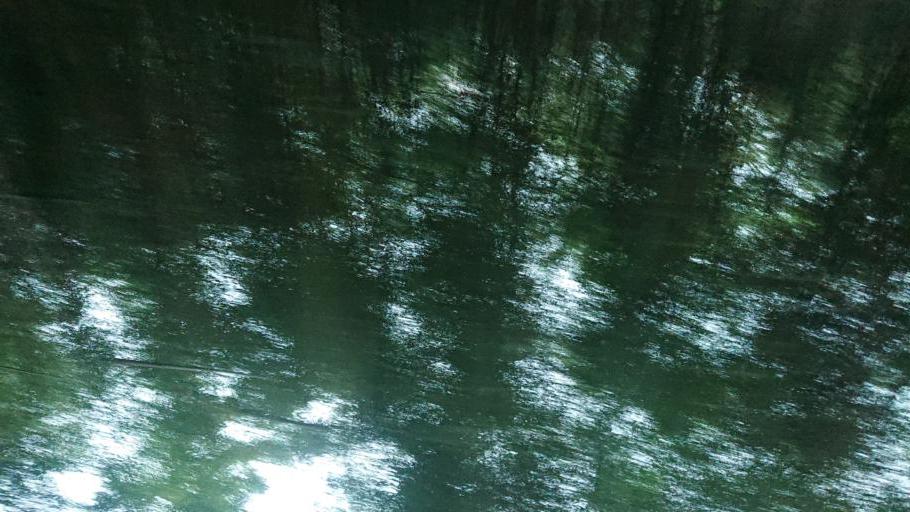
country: TW
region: Taiwan
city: Lugu
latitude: 23.5842
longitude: 120.7247
